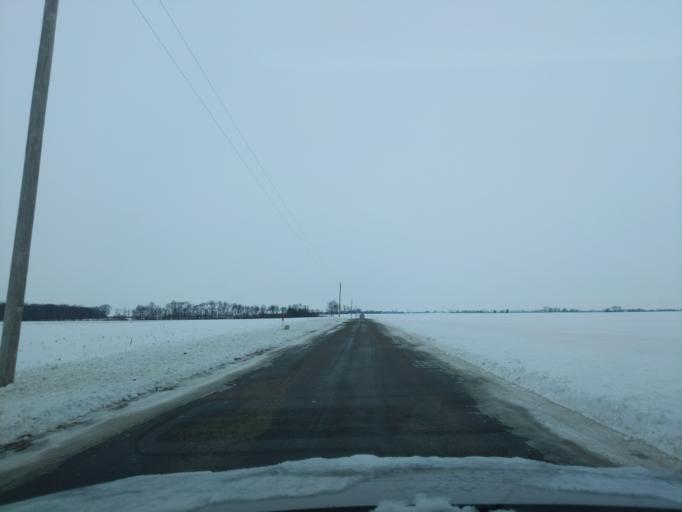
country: US
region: Indiana
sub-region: Benton County
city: Otterbein
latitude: 40.4531
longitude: -87.0933
